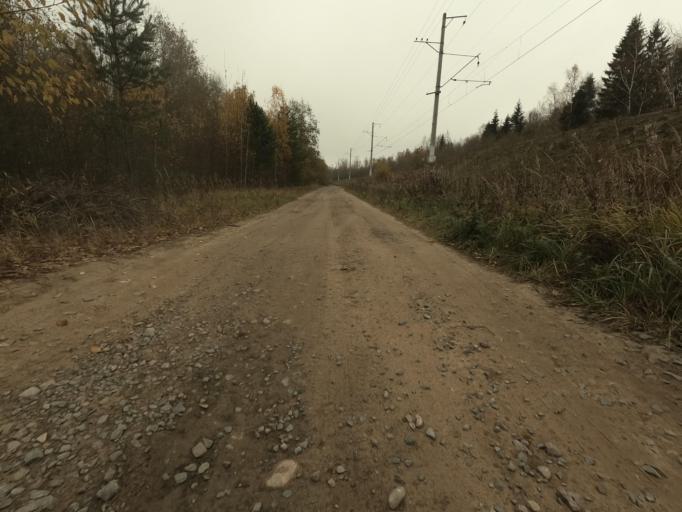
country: RU
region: Leningrad
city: Pavlovo
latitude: 59.7823
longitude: 30.8956
